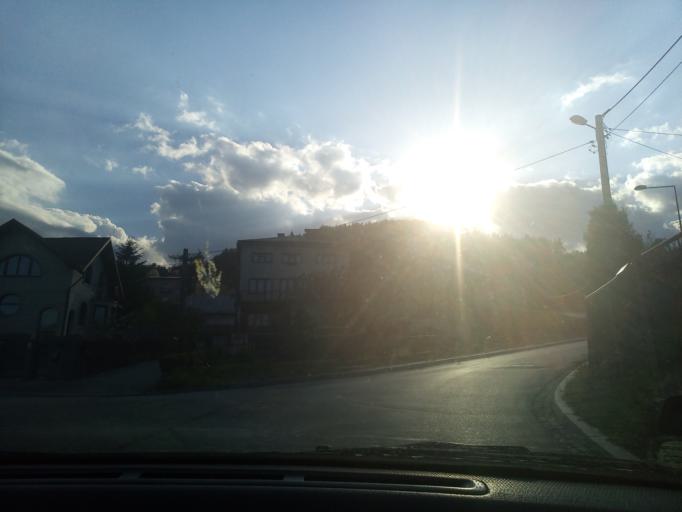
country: PL
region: Lesser Poland Voivodeship
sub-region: Powiat nowosadecki
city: Krynica-Zdroj
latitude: 49.4067
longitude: 20.9514
